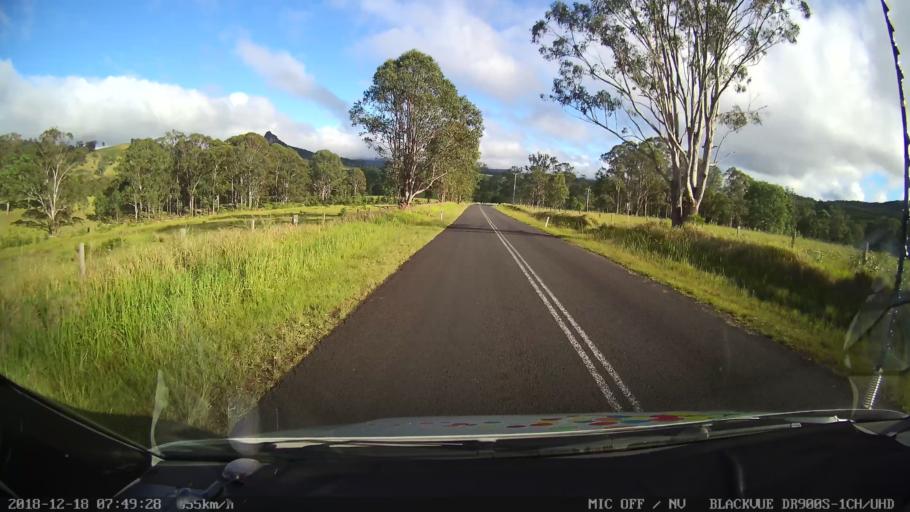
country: AU
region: New South Wales
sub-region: Kyogle
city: Kyogle
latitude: -28.4537
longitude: 152.5707
